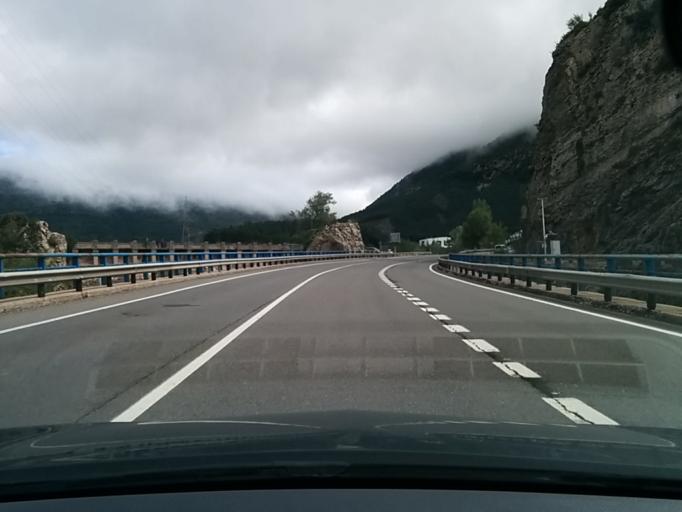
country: ES
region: Aragon
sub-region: Provincia de Huesca
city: Arguis
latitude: 42.3031
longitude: -0.4290
